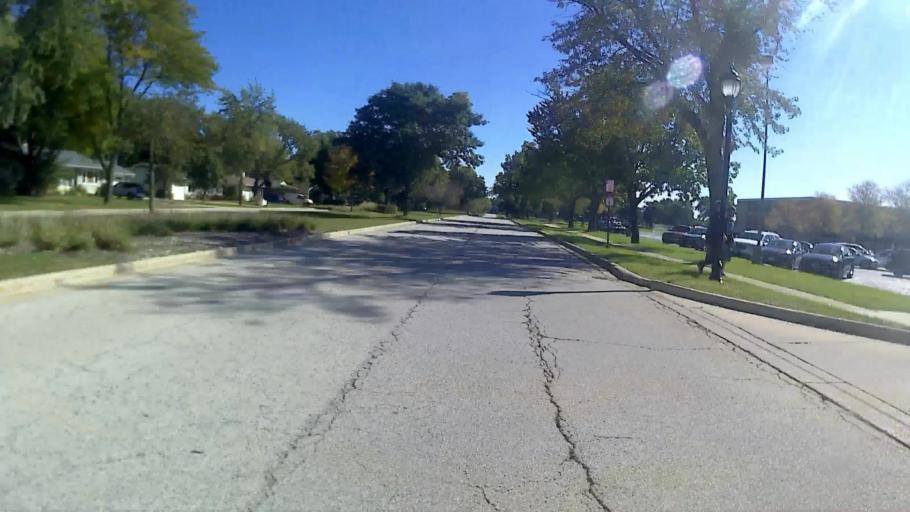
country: US
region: Illinois
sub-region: Cook County
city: Elk Grove Village
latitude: 42.0121
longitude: -87.9967
